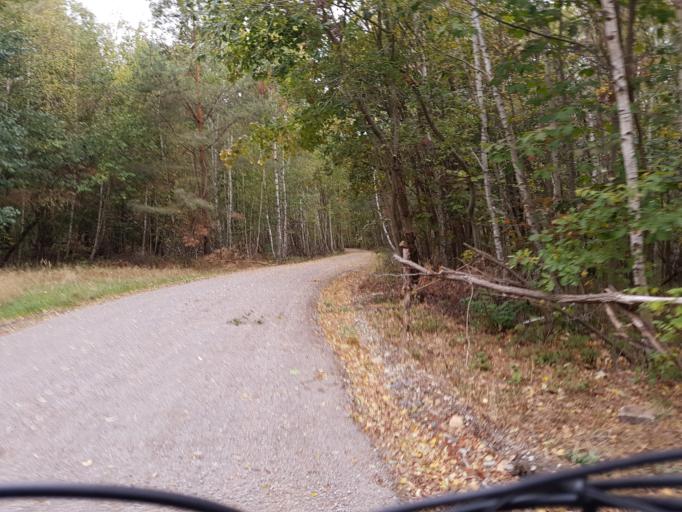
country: DE
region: Brandenburg
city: Trobitz
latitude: 51.5835
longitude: 13.4297
